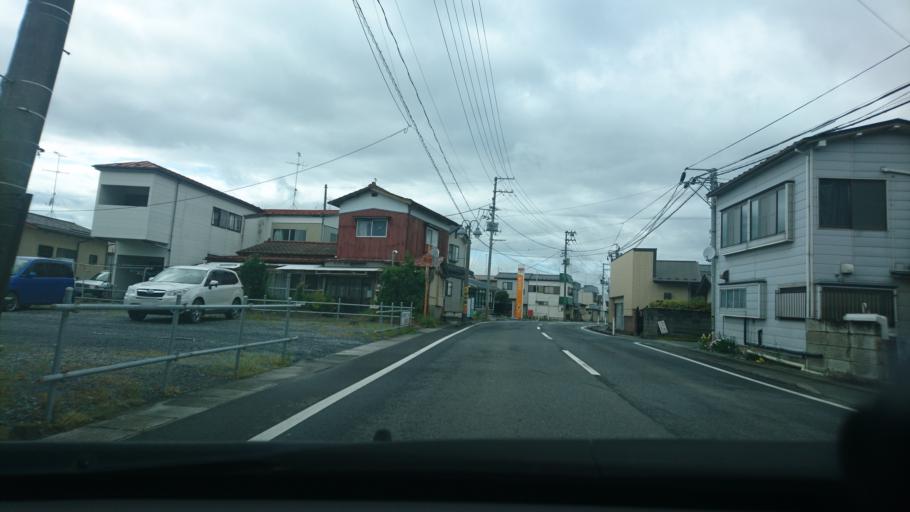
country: JP
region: Miyagi
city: Wakuya
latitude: 38.6099
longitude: 141.3004
